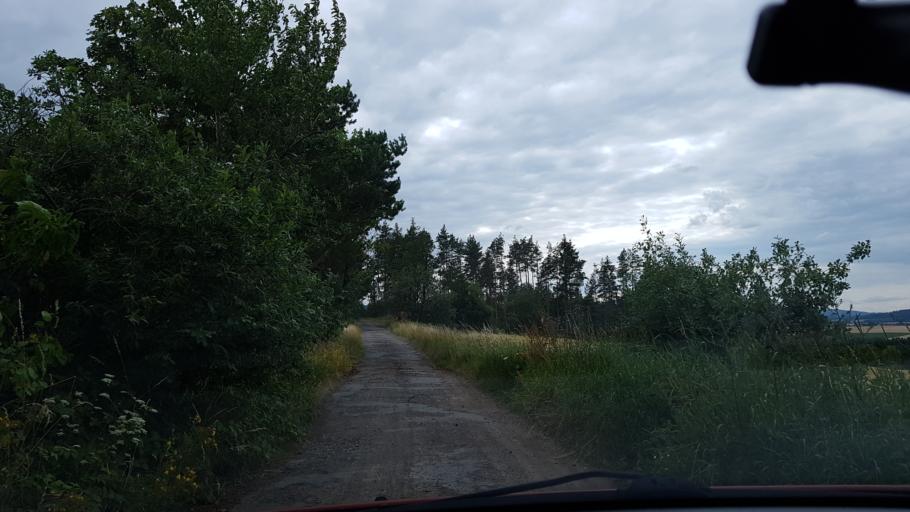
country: PL
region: Lower Silesian Voivodeship
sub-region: Powiat zabkowicki
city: Stoszowice
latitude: 50.5622
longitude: 16.7562
